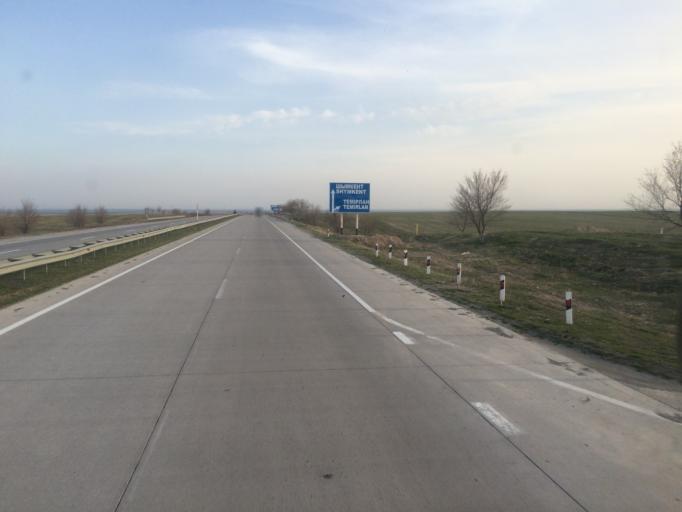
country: KZ
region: Ongtustik Qazaqstan
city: Temirlanovka
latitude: 42.6583
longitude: 69.2326
